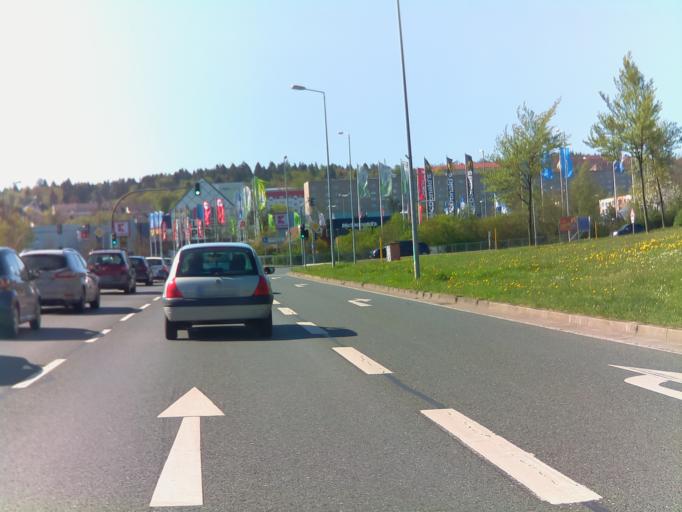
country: DE
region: Saxony
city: Plauen
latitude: 50.4989
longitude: 12.1715
